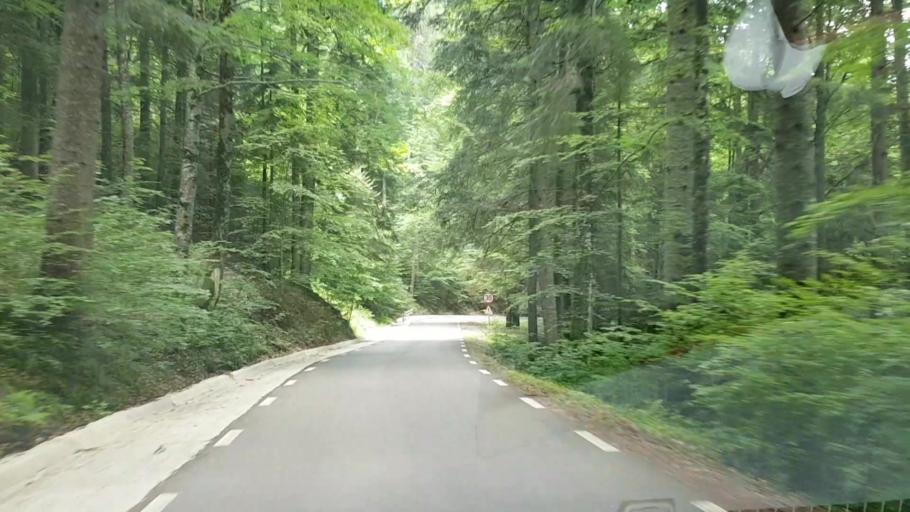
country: RO
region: Suceava
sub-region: Comuna Crucea
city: Crucea
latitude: 47.4326
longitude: 25.5734
